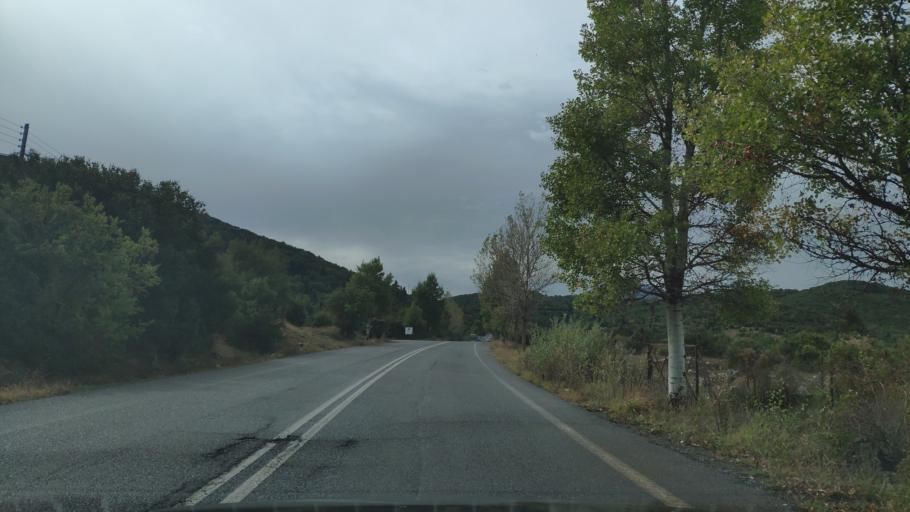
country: GR
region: Peloponnese
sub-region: Nomos Arkadias
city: Langadhia
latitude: 37.6889
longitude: 22.1946
